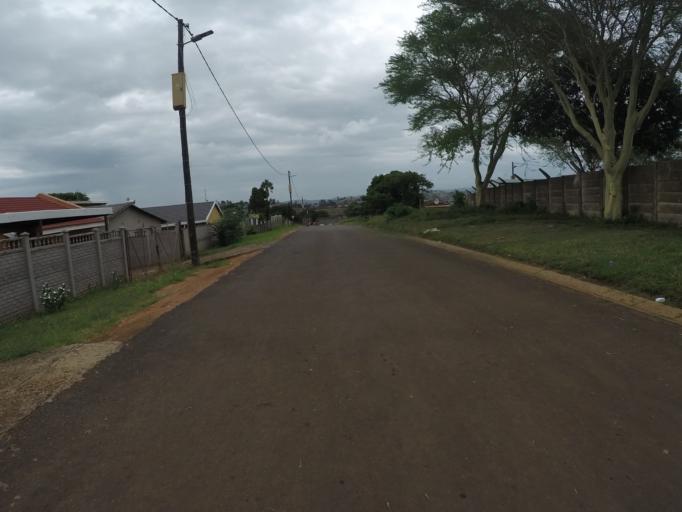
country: ZA
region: KwaZulu-Natal
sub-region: uThungulu District Municipality
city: Empangeni
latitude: -28.7764
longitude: 31.8622
